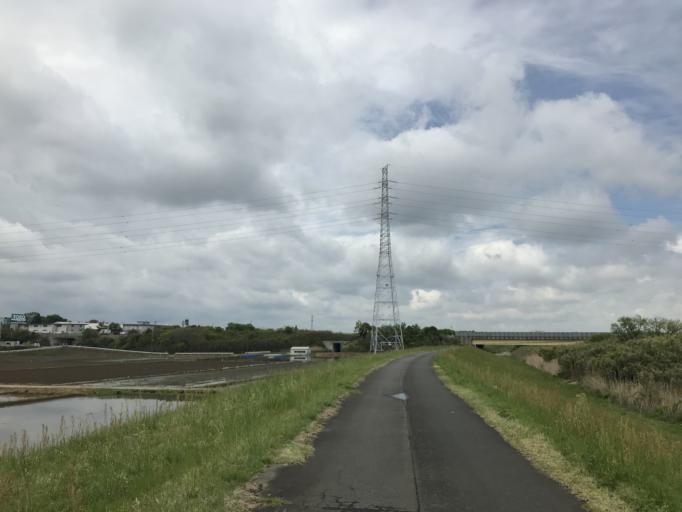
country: JP
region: Ibaraki
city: Mitsukaido
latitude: 35.9761
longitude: 139.9938
